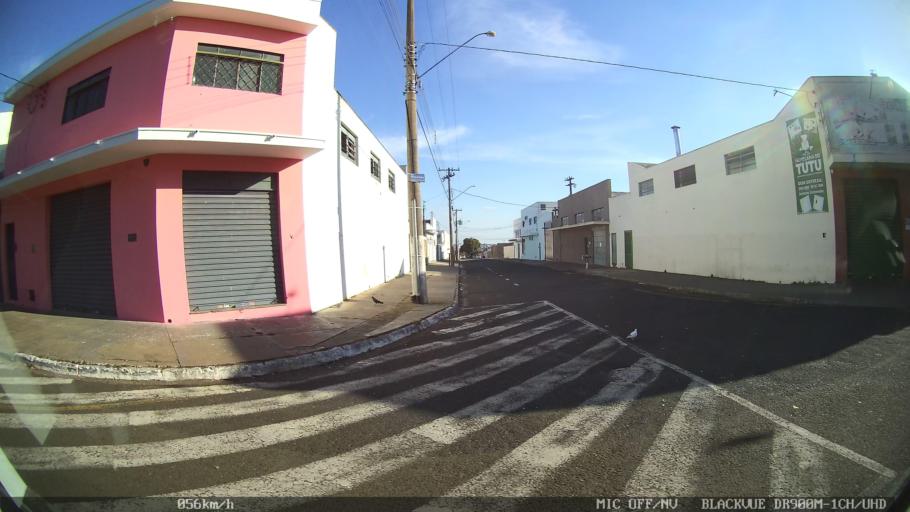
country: BR
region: Sao Paulo
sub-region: Franca
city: Franca
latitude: -20.5121
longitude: -47.3893
